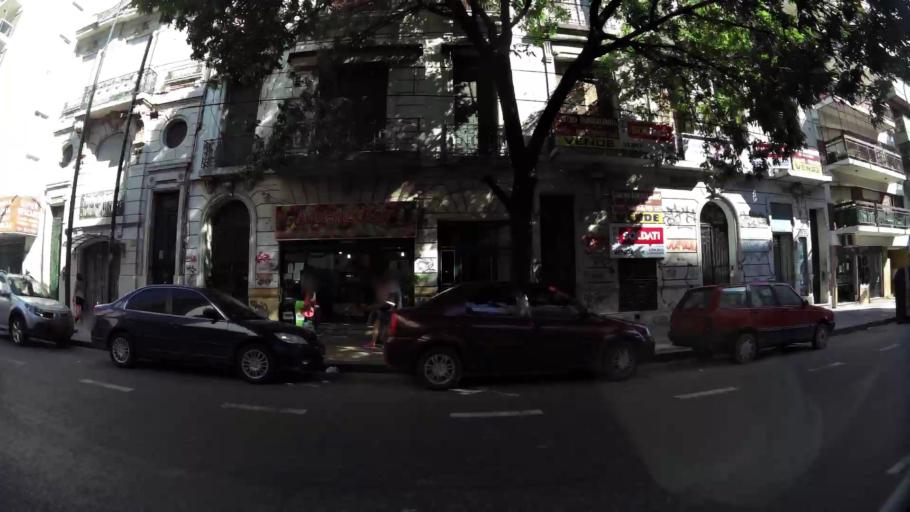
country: AR
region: Buenos Aires F.D.
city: Colegiales
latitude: -34.6131
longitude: -58.4246
